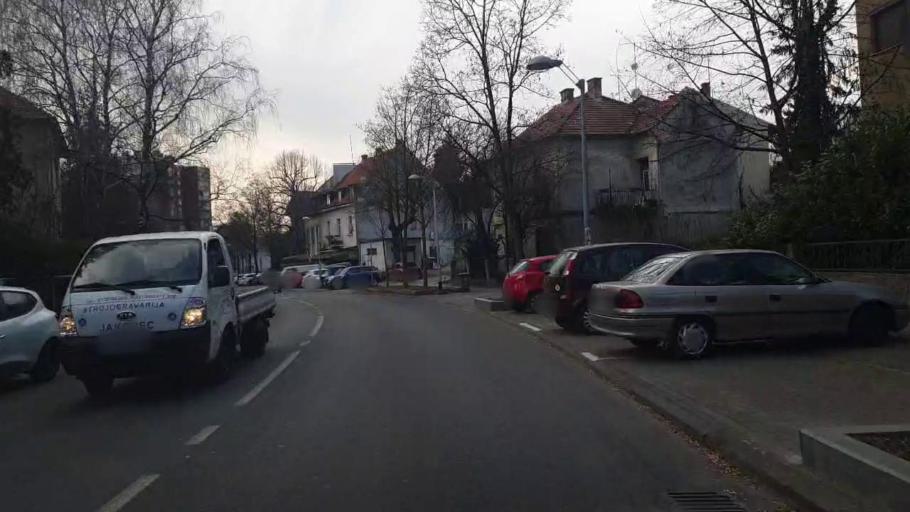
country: HR
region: Grad Zagreb
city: Zagreb
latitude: 45.8223
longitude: 16.0098
